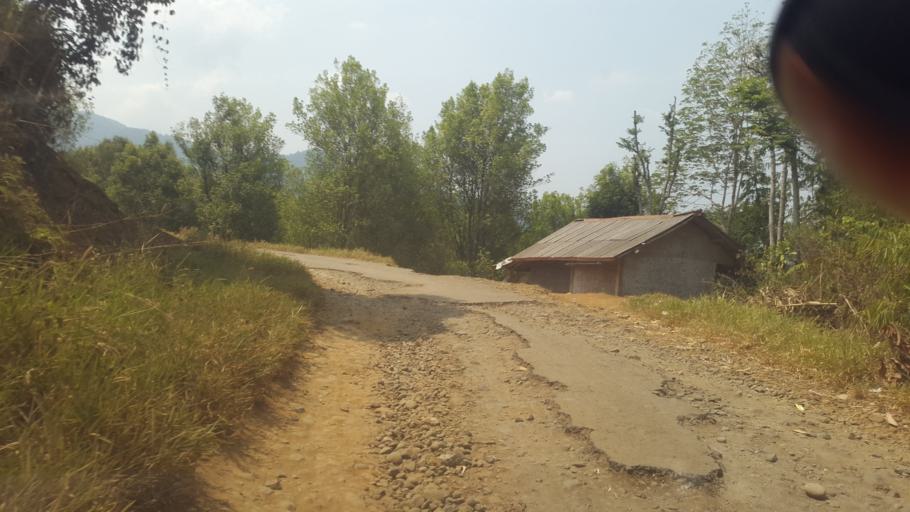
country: ID
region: West Java
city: Nagrak
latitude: -6.9006
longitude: 106.5242
